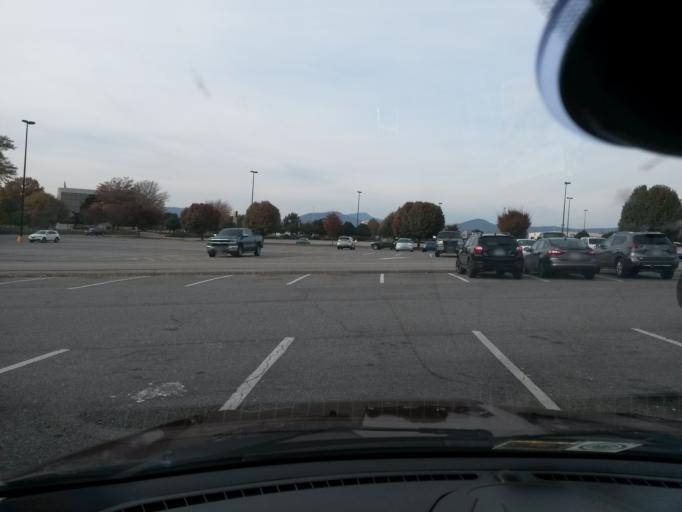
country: US
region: Virginia
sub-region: City of Roanoke
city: Roanoke
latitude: 37.3035
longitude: -79.9657
